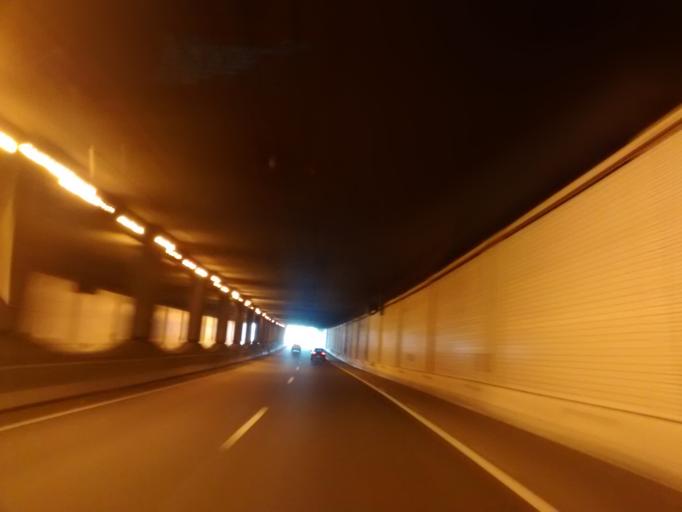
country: ES
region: Cantabria
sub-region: Provincia de Cantabria
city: El Astillero
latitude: 43.4010
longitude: -3.8163
